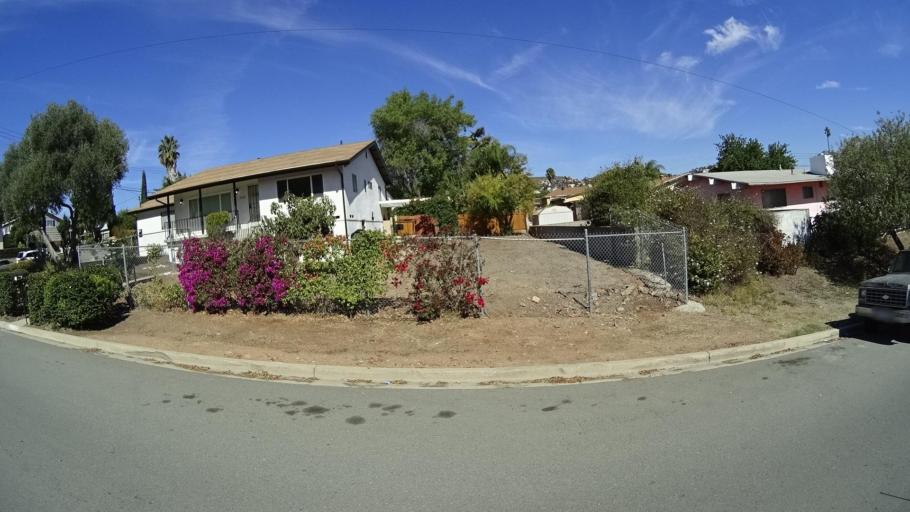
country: US
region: California
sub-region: San Diego County
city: La Presa
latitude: 32.7060
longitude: -116.9946
